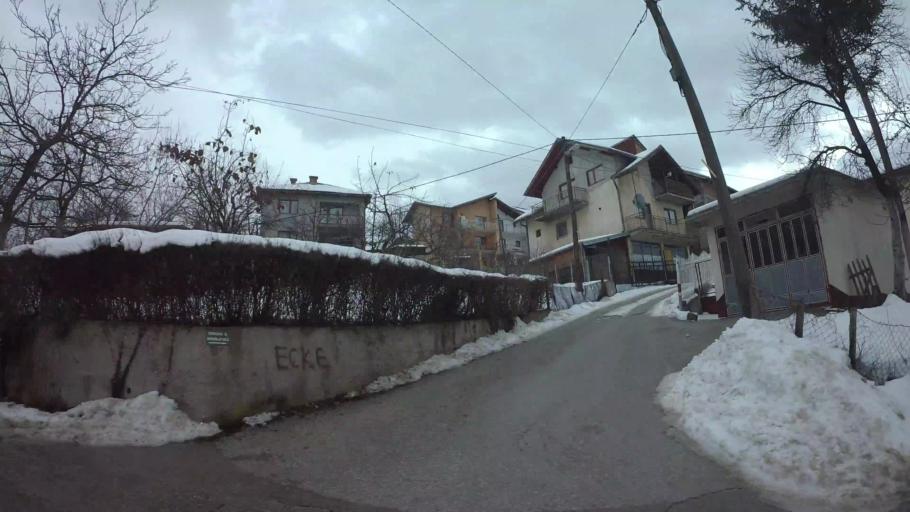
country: BA
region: Federation of Bosnia and Herzegovina
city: Vogosca
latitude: 43.8683
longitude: 18.3183
